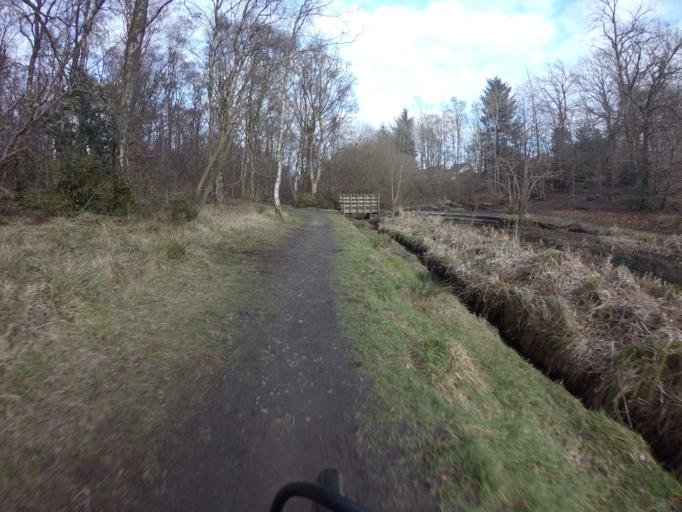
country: GB
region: Scotland
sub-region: West Lothian
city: Livingston
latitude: 55.8687
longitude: -3.5199
